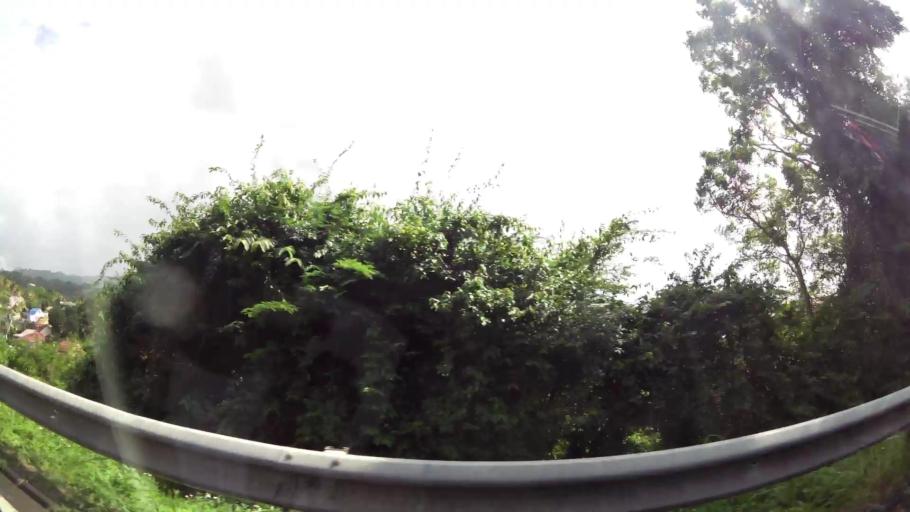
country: GP
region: Guadeloupe
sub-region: Guadeloupe
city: Basse-Terre
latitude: 16.0057
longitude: -61.7187
